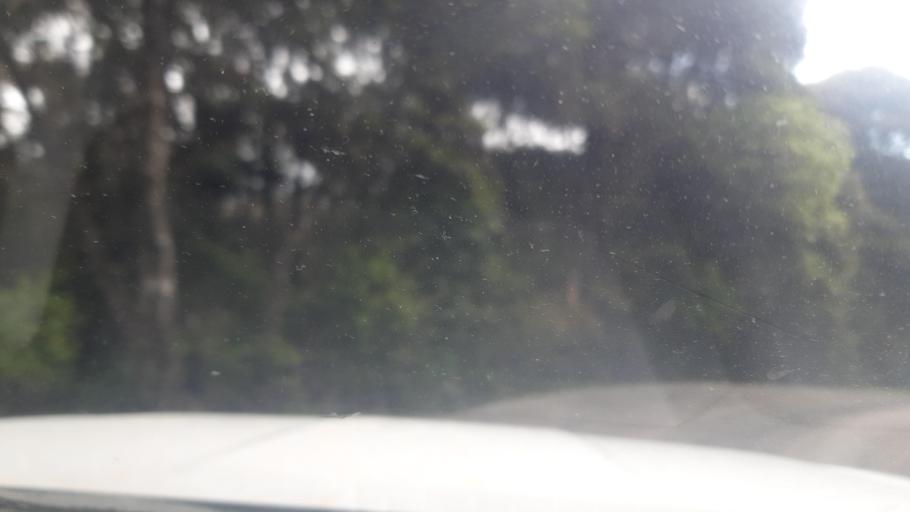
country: NZ
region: Northland
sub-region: Far North District
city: Taipa
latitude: -35.0666
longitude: 173.5271
